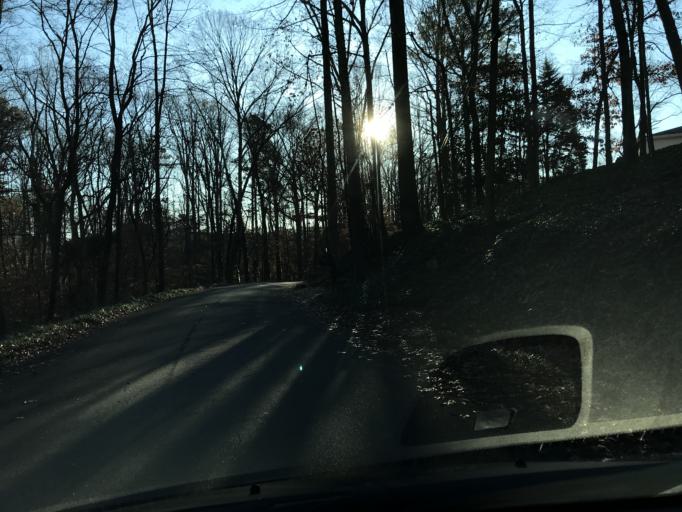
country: US
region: Georgia
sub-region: DeKalb County
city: North Atlanta
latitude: 33.8840
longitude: -84.3326
